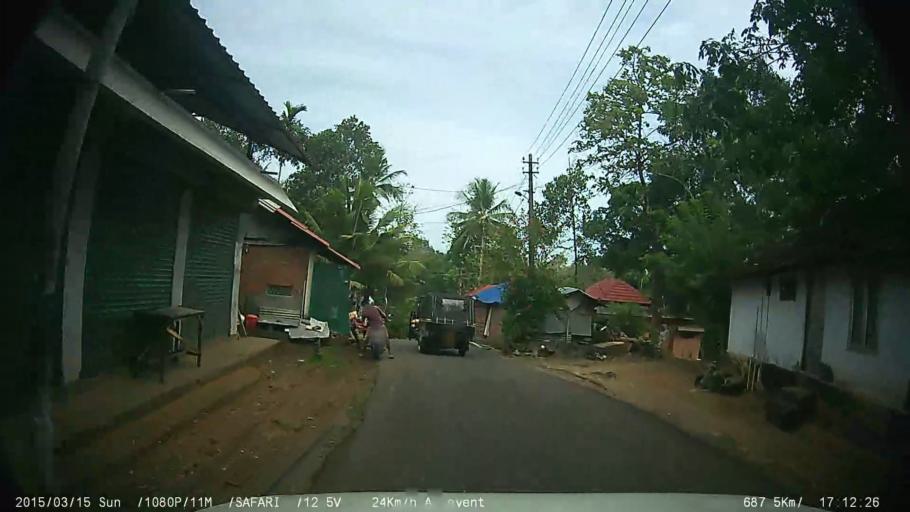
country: IN
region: Kerala
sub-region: Kottayam
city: Palackattumala
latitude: 9.8558
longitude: 76.6806
